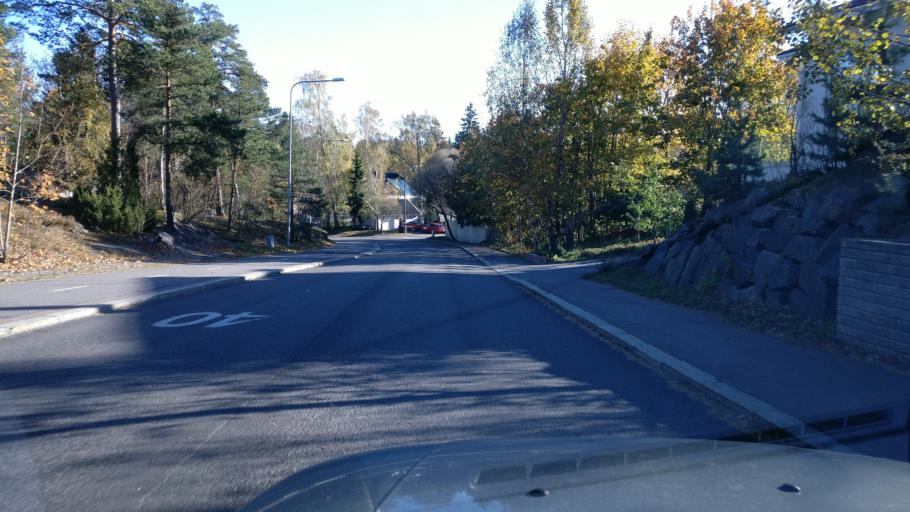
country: FI
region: Uusimaa
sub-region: Helsinki
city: Helsinki
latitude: 60.1645
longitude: 25.0676
